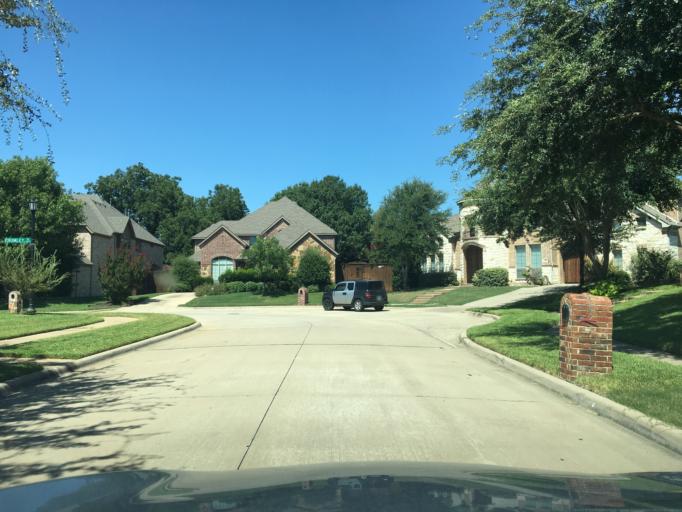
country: US
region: Texas
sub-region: Dallas County
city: Sachse
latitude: 32.9677
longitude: -96.6157
